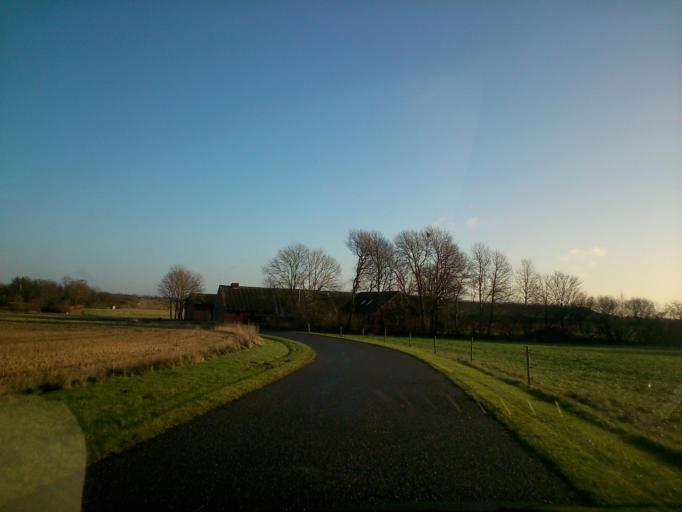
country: DK
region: Central Jutland
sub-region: Ringkobing-Skjern Kommune
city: Skjern
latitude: 55.9760
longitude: 8.5605
